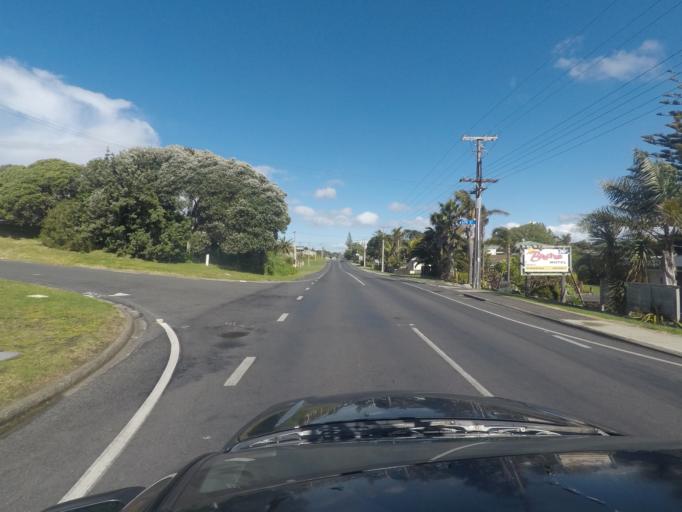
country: NZ
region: Bay of Plenty
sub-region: Western Bay of Plenty District
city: Waihi Beach
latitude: -37.4152
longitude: 175.9476
